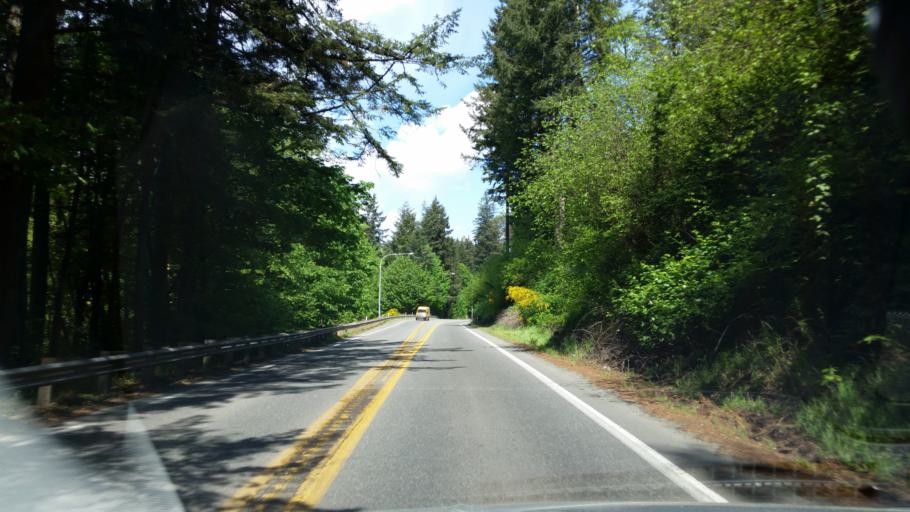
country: US
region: Washington
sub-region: Pierce County
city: Wauna
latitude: 47.3792
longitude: -122.6532
